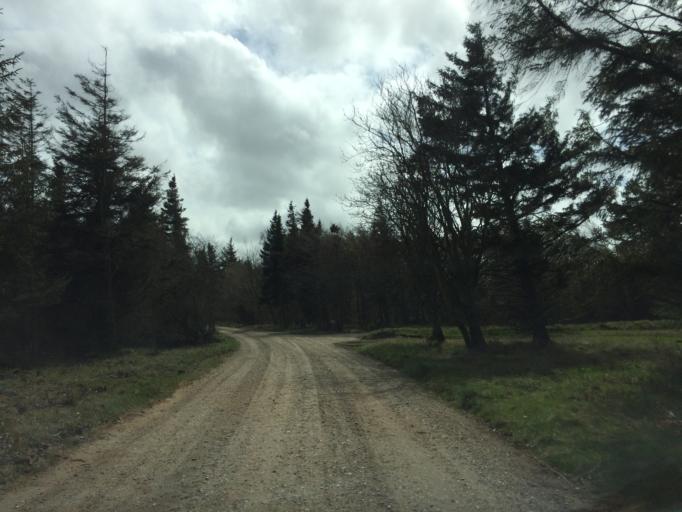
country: DK
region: South Denmark
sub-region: Varde Kommune
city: Oksbol
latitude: 55.5672
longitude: 8.3098
